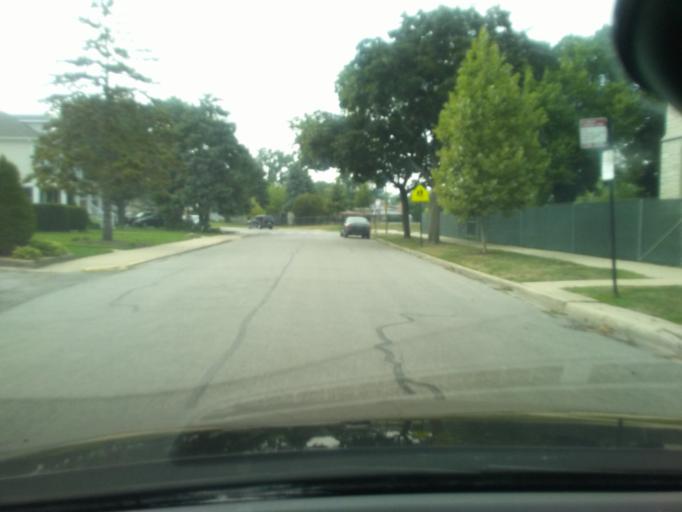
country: US
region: Illinois
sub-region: Cook County
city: Lincolnwood
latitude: 41.9939
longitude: -87.7455
